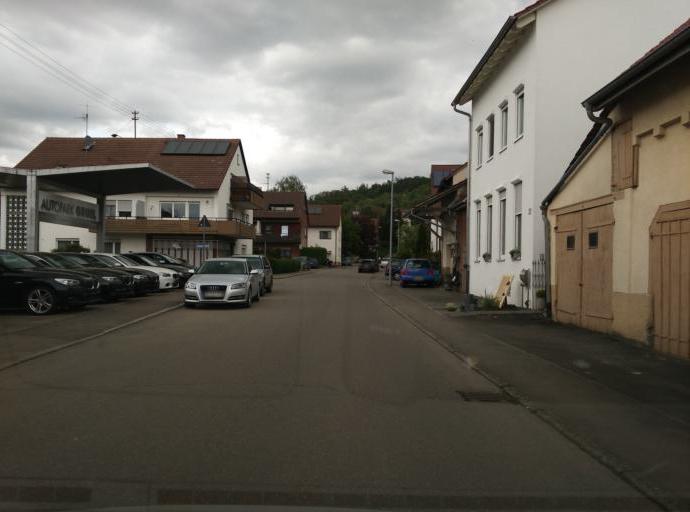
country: DE
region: Baden-Wuerttemberg
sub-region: Regierungsbezirk Stuttgart
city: Frickenhausen
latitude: 48.5948
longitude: 9.3622
